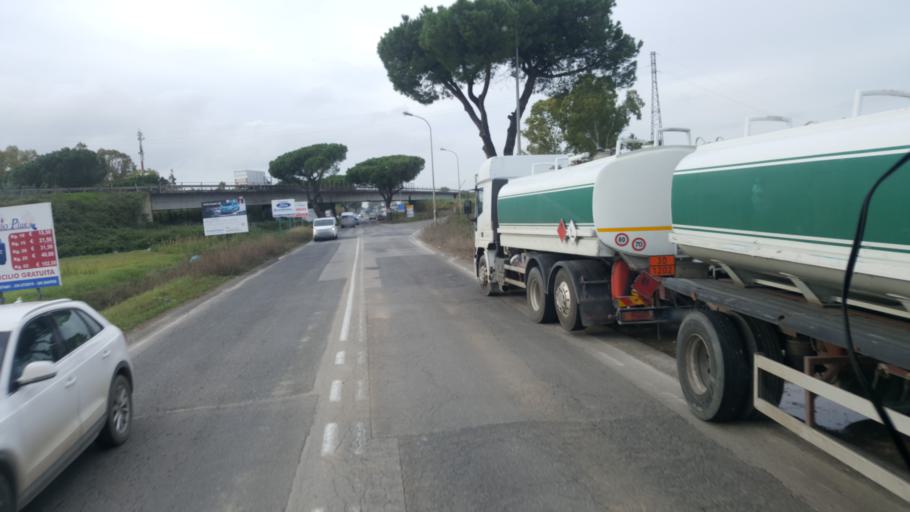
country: IT
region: Latium
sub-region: Provincia di Latina
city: Borgo Podgora
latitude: 41.4828
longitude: 12.8615
